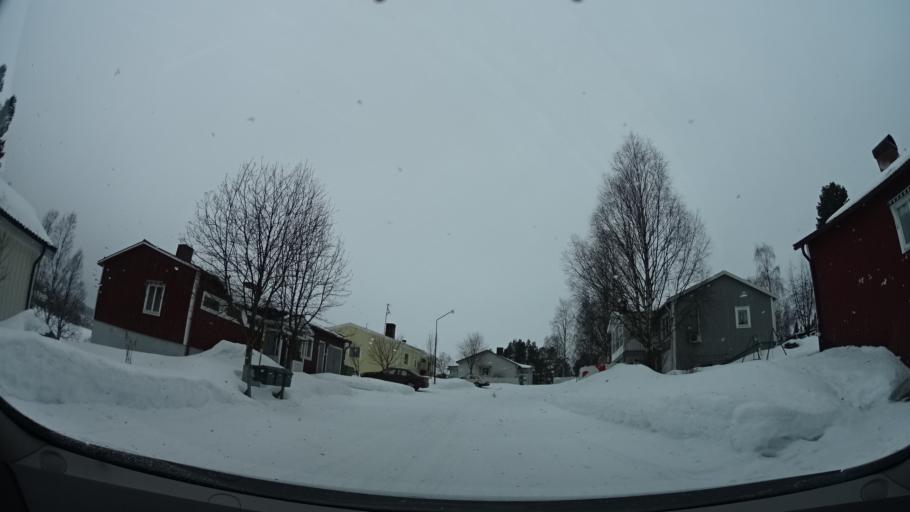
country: SE
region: Vaesterbotten
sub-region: Mala Kommun
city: Mala
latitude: 65.1761
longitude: 18.7518
